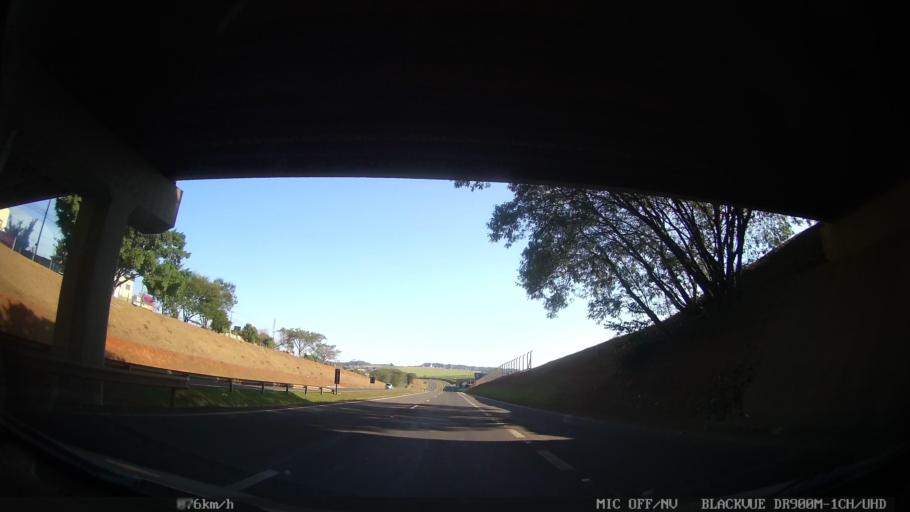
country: BR
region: Sao Paulo
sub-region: Piracicaba
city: Piracicaba
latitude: -22.6736
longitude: -47.6303
